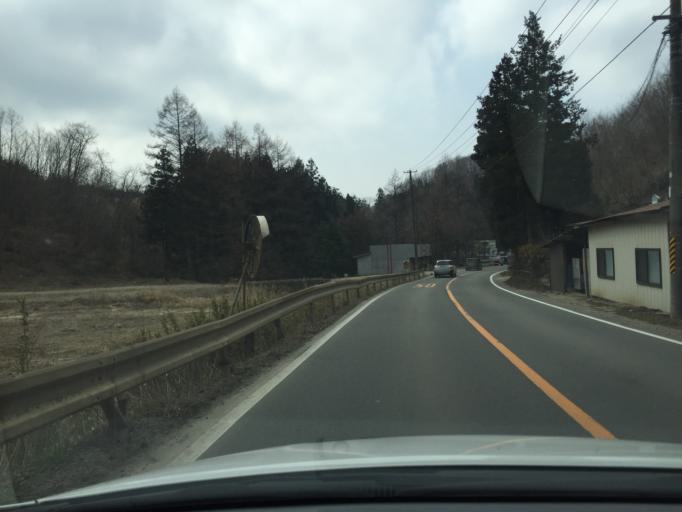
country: JP
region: Fukushima
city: Yanagawamachi-saiwaicho
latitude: 37.7550
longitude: 140.7004
